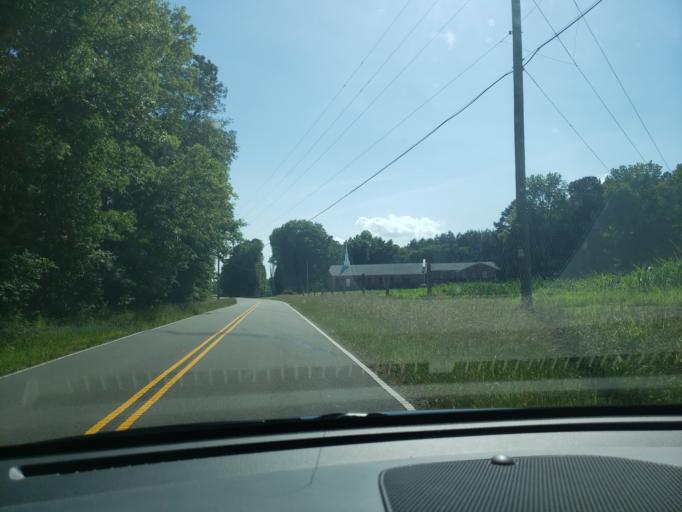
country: US
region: North Carolina
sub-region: Durham County
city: Gorman
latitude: 36.1239
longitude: -78.8936
